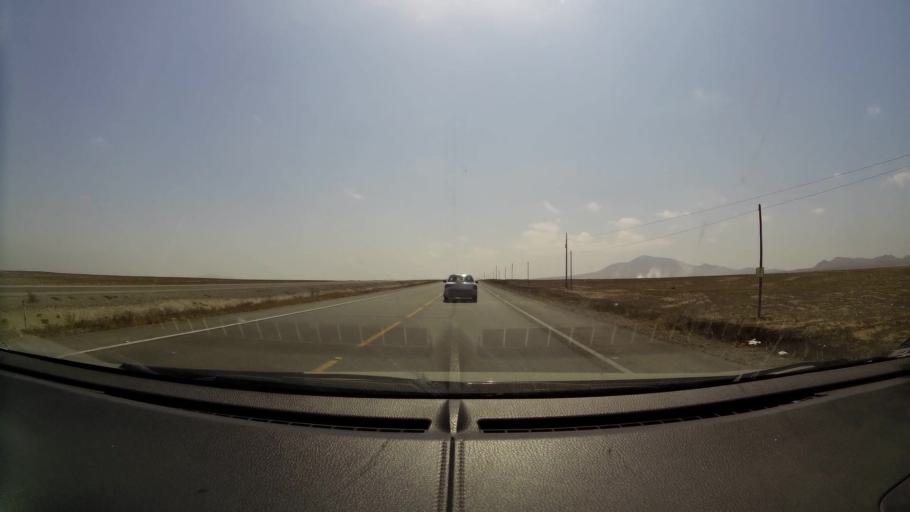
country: PE
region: Lambayeque
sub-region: Provincia de Chiclayo
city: Mocupe
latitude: -6.9420
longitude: -79.7184
